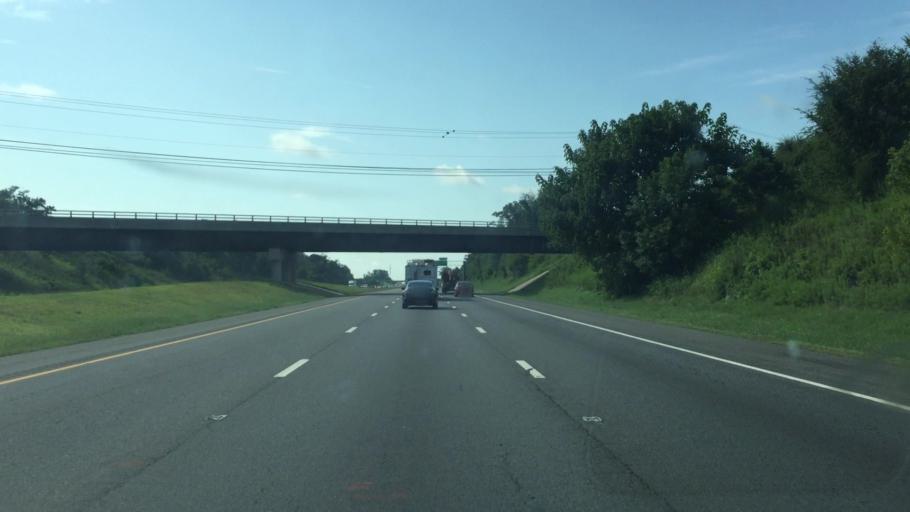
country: US
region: North Carolina
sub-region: Cabarrus County
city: Harrisburg
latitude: 35.2971
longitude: -80.6833
